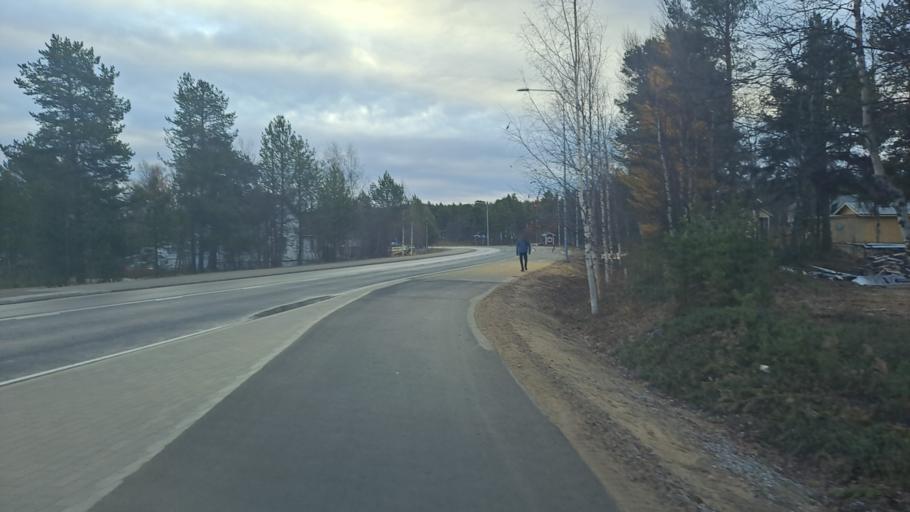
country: FI
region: Lapland
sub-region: Pohjois-Lappi
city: Inari
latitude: 68.9032
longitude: 27.0332
